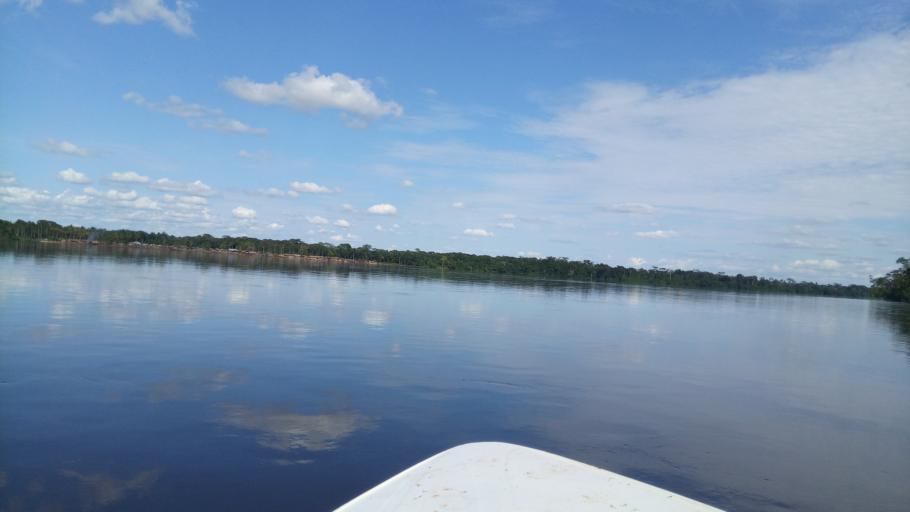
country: CD
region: Eastern Province
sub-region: Sous-Region de la Tshopo
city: Yangambi
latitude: 0.5520
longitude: 24.2426
